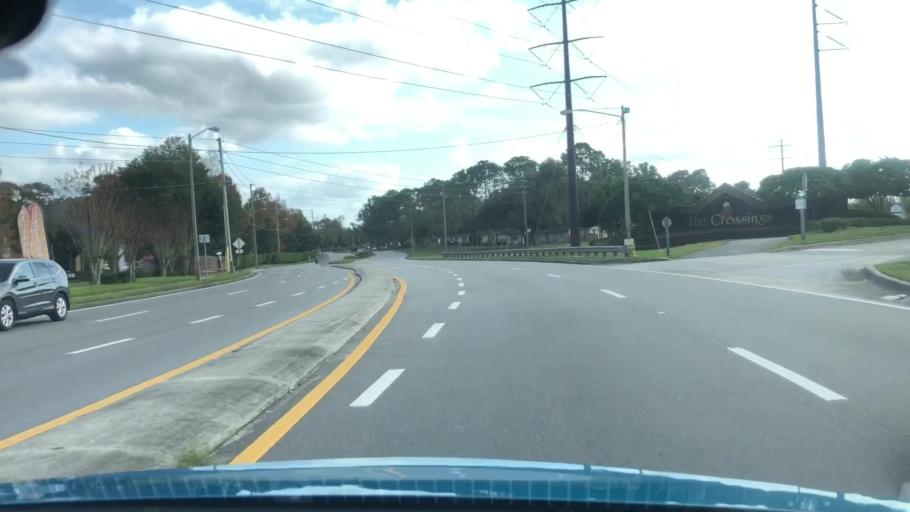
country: US
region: Florida
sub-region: Seminole County
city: Heathrow
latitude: 28.7523
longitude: -81.3470
